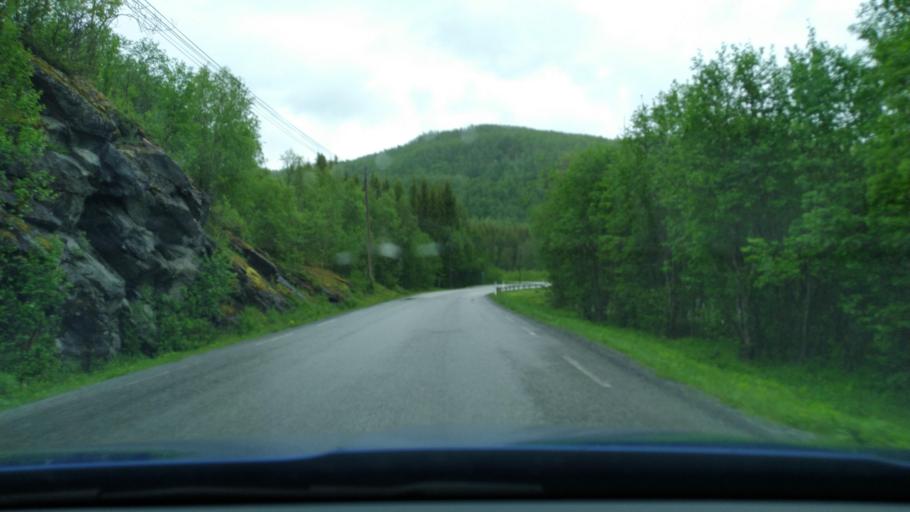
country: NO
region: Troms
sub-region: Dyroy
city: Brostadbotn
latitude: 69.0717
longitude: 17.7290
